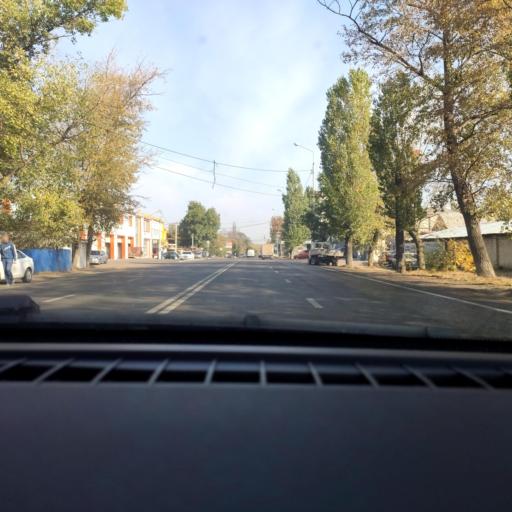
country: RU
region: Voronezj
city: Maslovka
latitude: 51.5971
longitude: 39.2521
